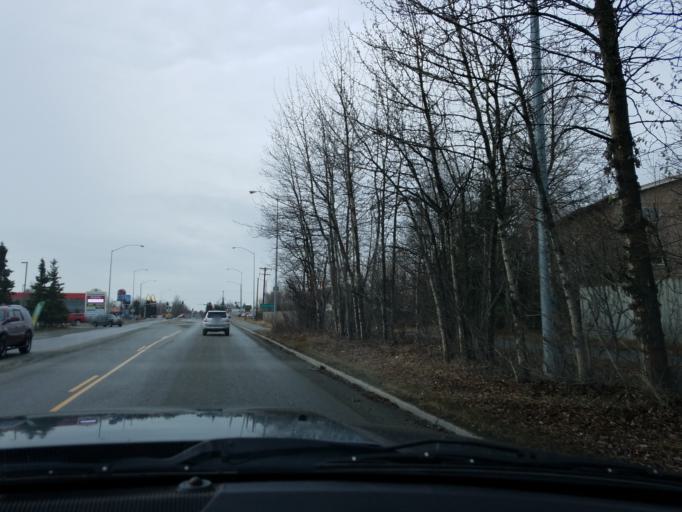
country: US
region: Alaska
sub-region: Anchorage Municipality
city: Anchorage
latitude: 61.1396
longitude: -149.9520
